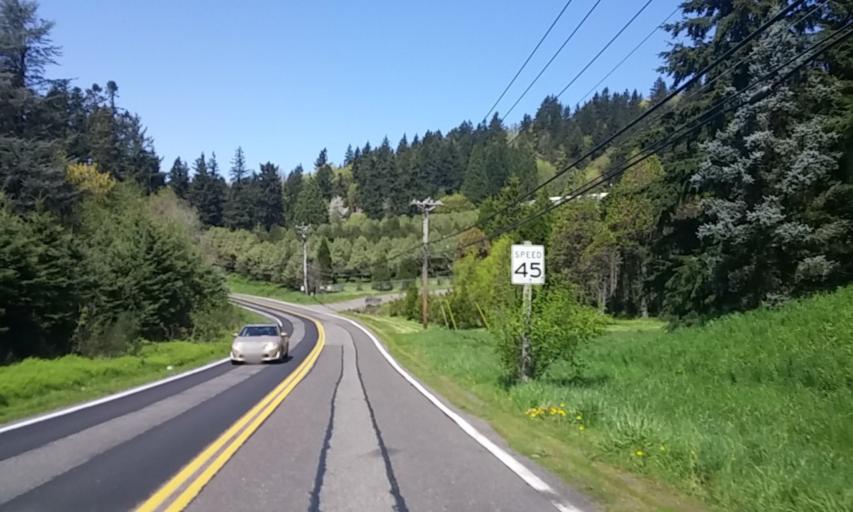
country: US
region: Oregon
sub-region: Washington County
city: West Haven-Sylvan
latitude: 45.5202
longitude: -122.7559
